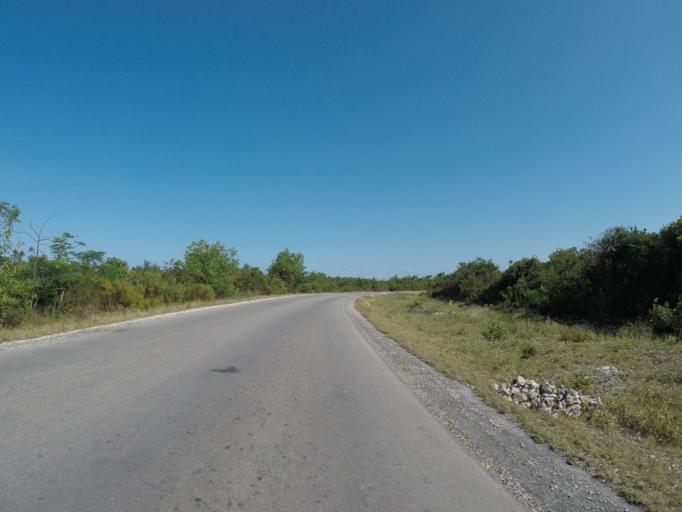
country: TZ
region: Zanzibar Central/South
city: Nganane
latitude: -6.2081
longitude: 39.5311
